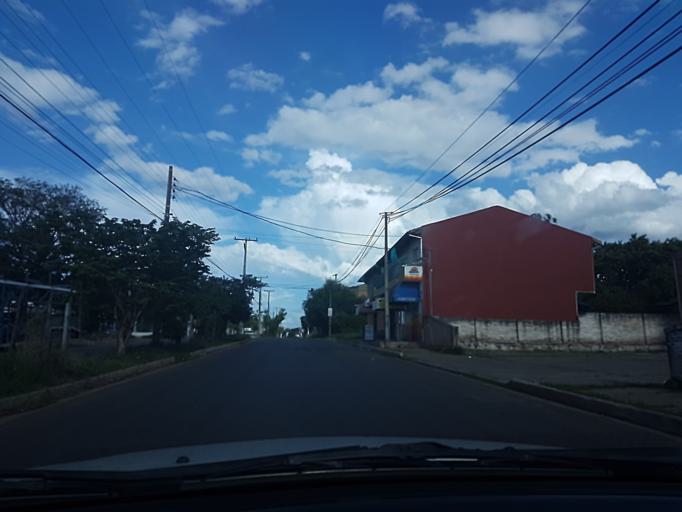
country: PY
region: Central
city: Colonia Mariano Roque Alonso
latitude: -25.2075
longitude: -57.5247
